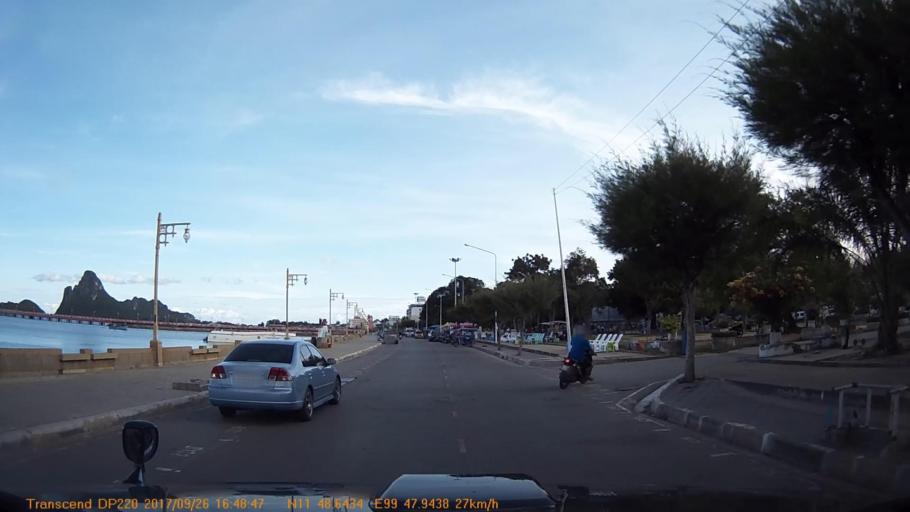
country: TH
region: Prachuap Khiri Khan
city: Prachuap Khiri Khan
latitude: 11.8107
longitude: 99.7991
